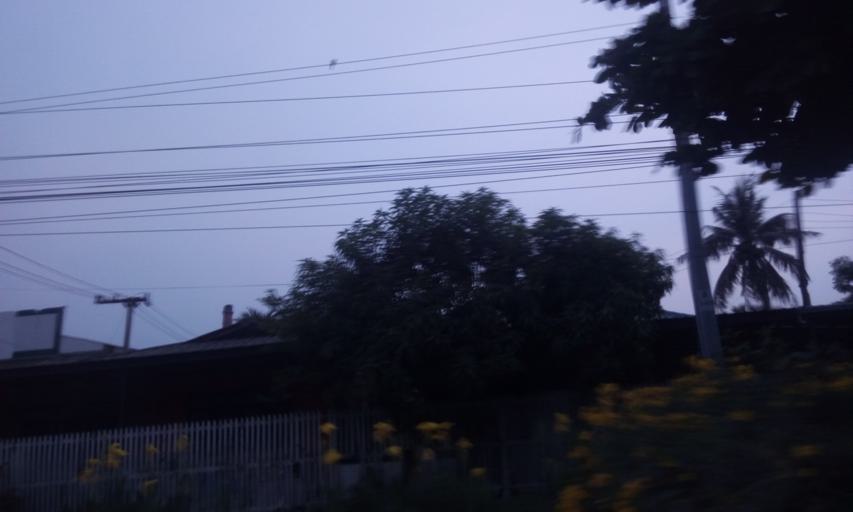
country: TH
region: Bangkok
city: Nong Chok
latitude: 13.8323
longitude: 100.9116
